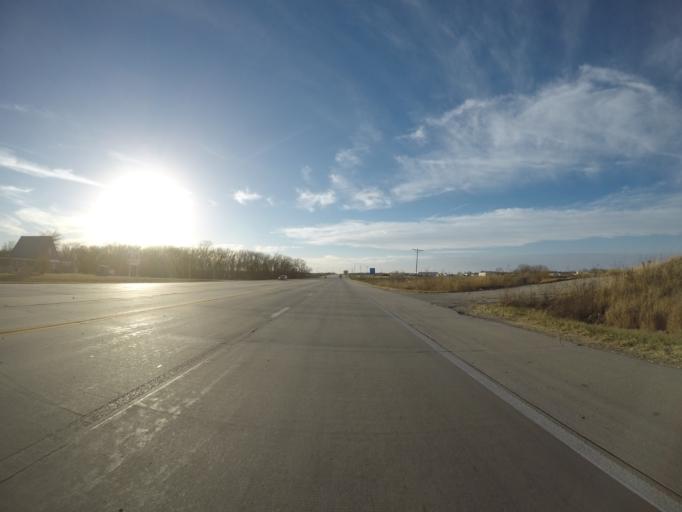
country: US
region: Kansas
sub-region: Lyon County
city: Emporia
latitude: 38.4123
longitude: -96.2404
